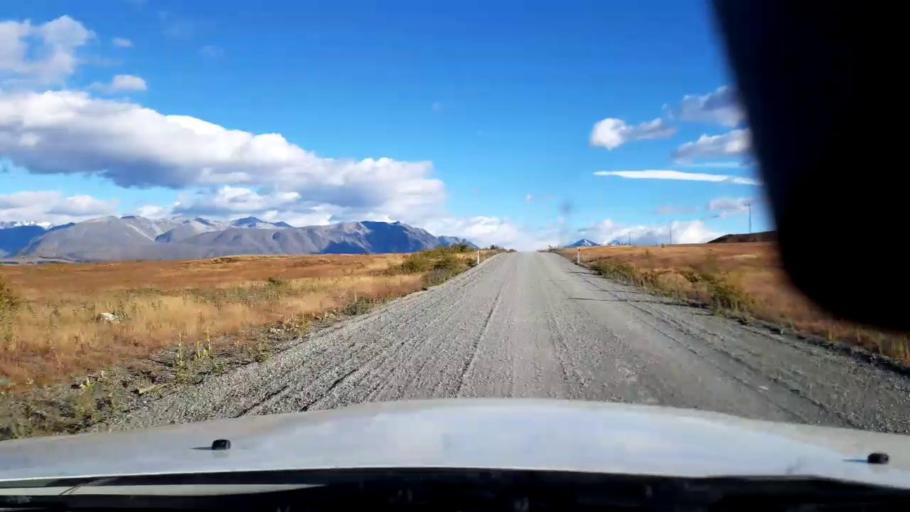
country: NZ
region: Canterbury
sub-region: Timaru District
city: Pleasant Point
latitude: -43.9232
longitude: 170.5598
